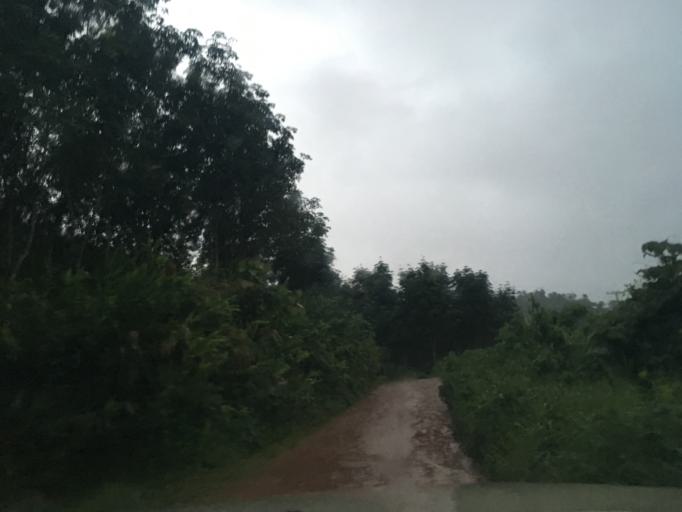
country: LA
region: Oudomxai
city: Muang La
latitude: 21.2493
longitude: 101.9331
